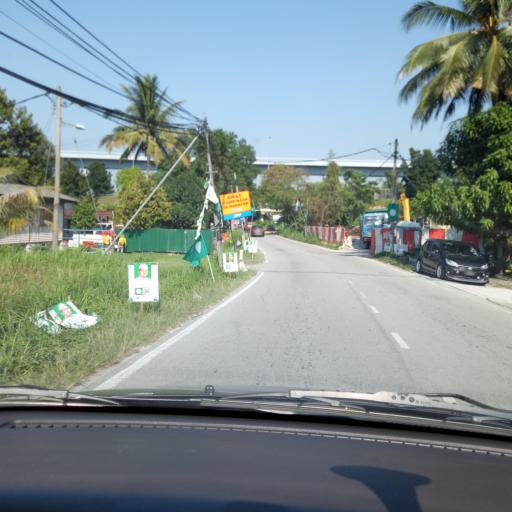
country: MY
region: Selangor
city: Kampong Baharu Balakong
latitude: 3.0162
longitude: 101.7754
